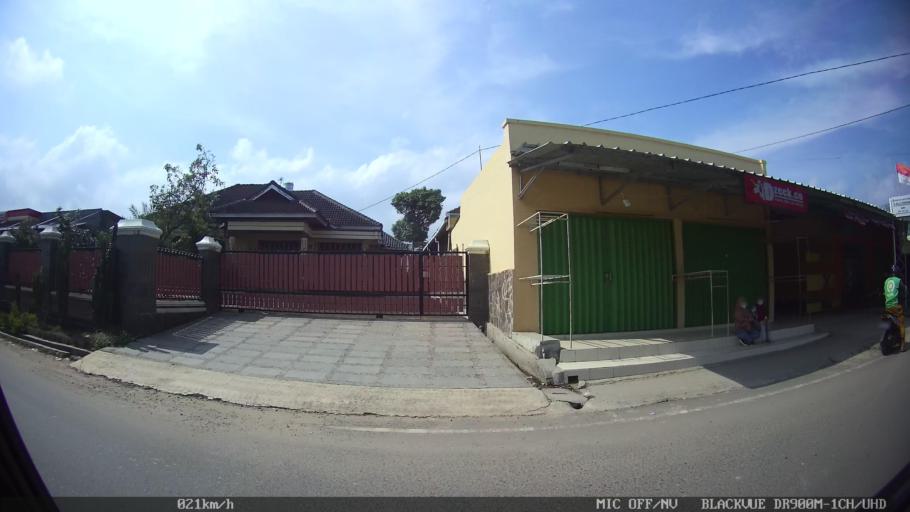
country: ID
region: Lampung
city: Kedaton
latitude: -5.3587
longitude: 105.2590
